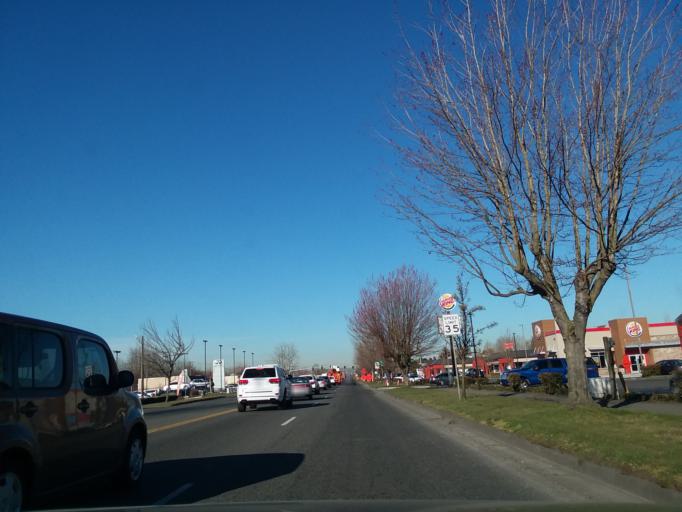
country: US
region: Washington
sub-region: Pierce County
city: Fife
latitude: 47.2431
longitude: -122.3618
